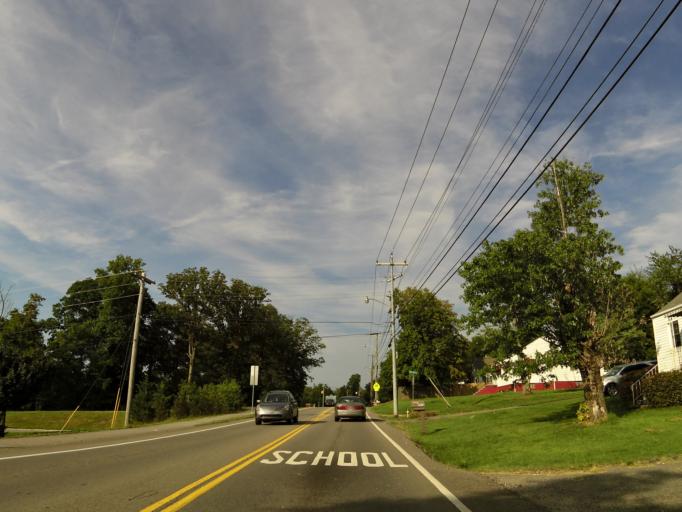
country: US
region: Tennessee
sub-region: Blount County
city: Maryville
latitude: 35.7609
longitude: -83.9491
